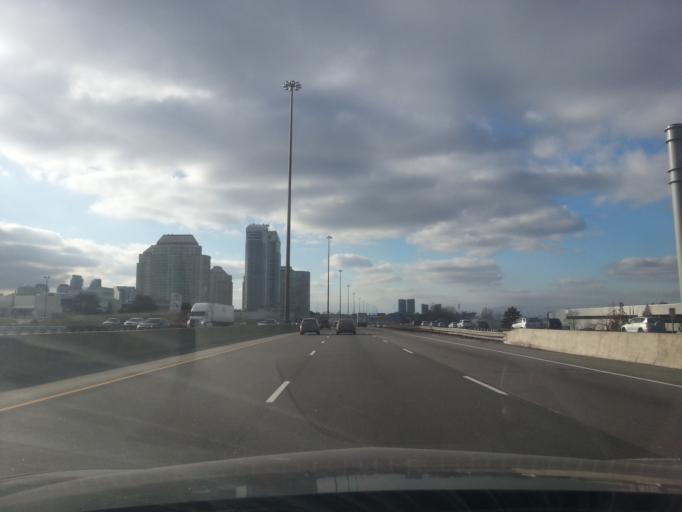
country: CA
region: Ontario
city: Scarborough
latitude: 43.7845
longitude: -79.2396
